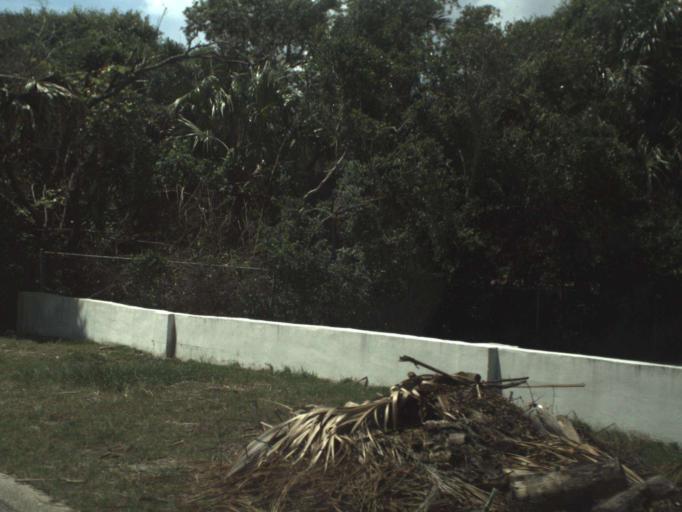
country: US
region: Florida
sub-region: Volusia County
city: Daytona Beach Shores
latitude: 29.1780
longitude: -80.9875
